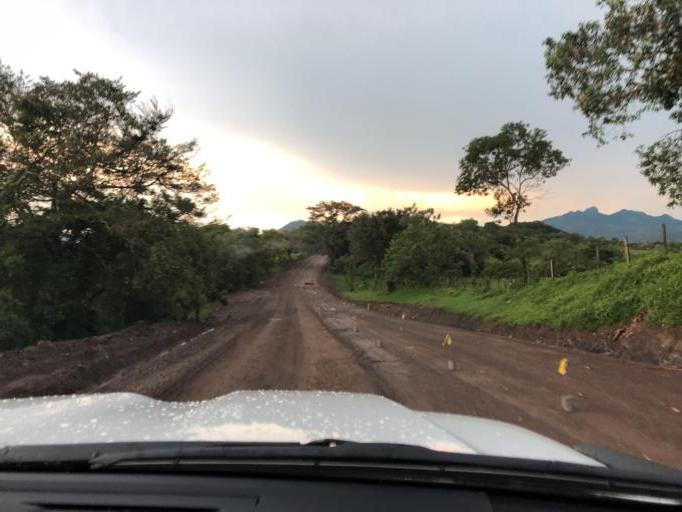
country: NI
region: Chontales
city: La Libertad
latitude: 12.2033
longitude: -85.1749
